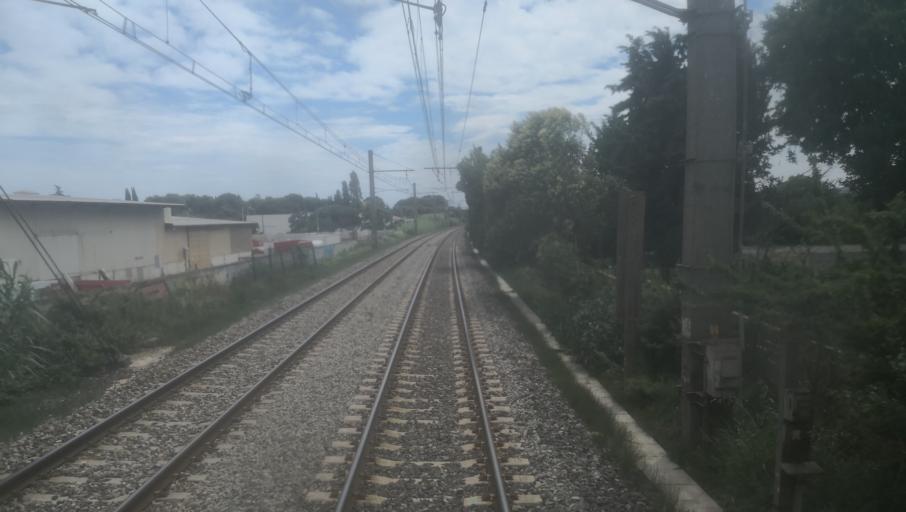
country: FR
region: Languedoc-Roussillon
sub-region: Departement de l'Herault
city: Montpellier
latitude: 43.5843
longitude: 3.8759
